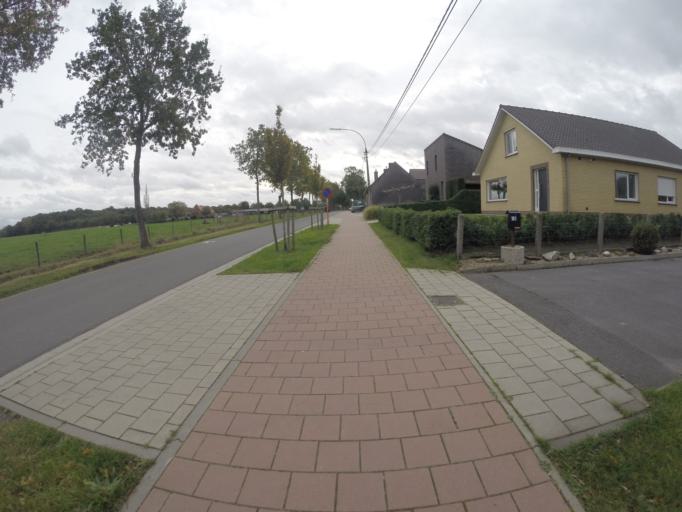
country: BE
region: Flanders
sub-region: Provincie Oost-Vlaanderen
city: Maldegem
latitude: 51.1732
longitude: 3.4515
